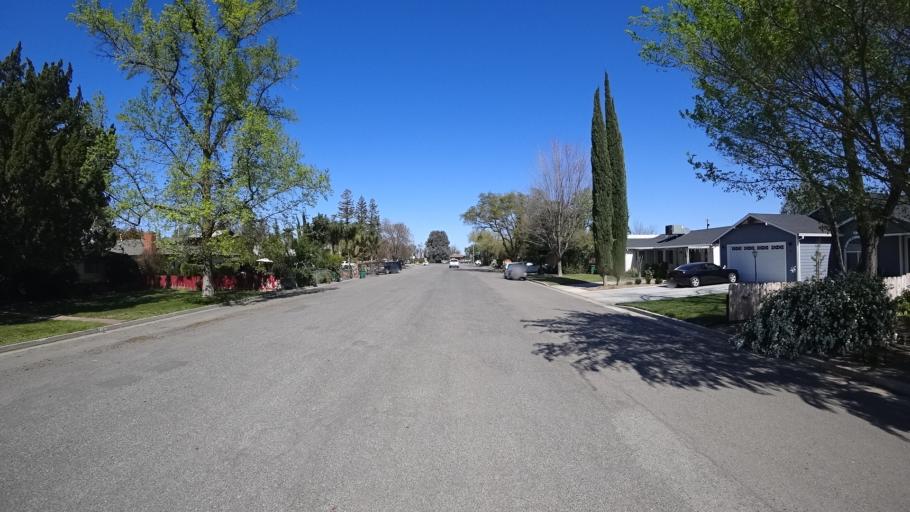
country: US
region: California
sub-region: Glenn County
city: Hamilton City
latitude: 39.7439
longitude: -122.0161
